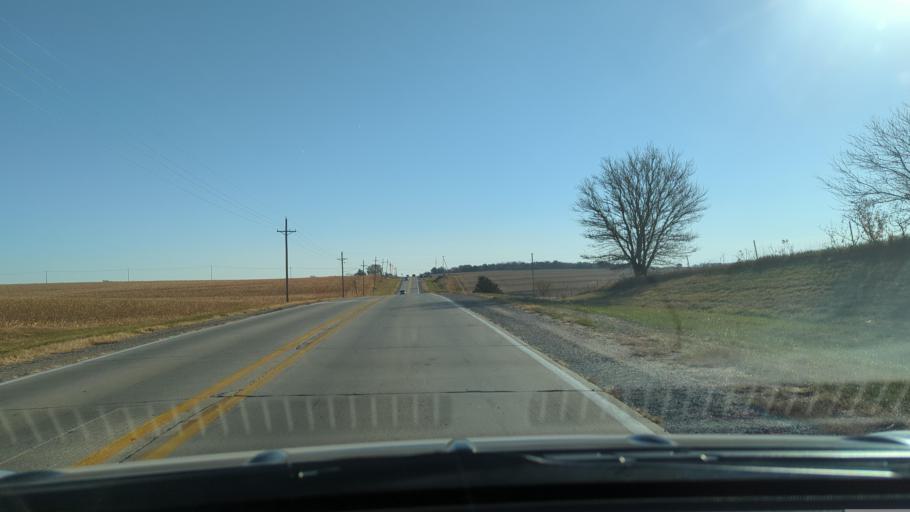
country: US
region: Nebraska
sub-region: Sarpy County
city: Papillion
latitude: 41.0925
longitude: -96.0306
